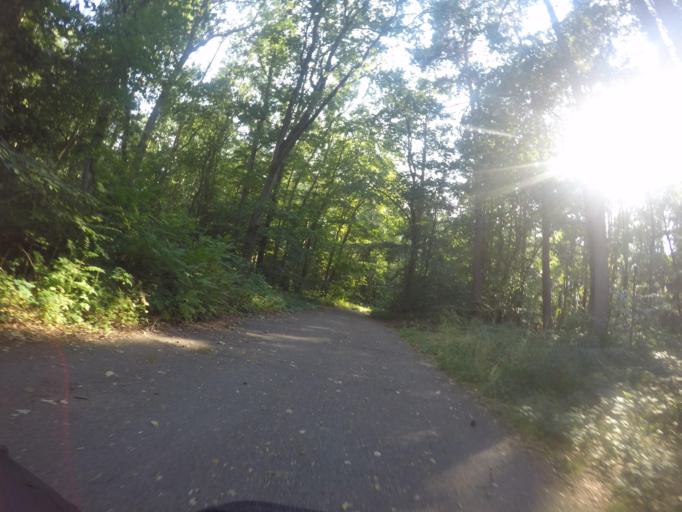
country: DE
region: Lower Saxony
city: Dahlenburg
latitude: 53.2056
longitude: 10.7303
